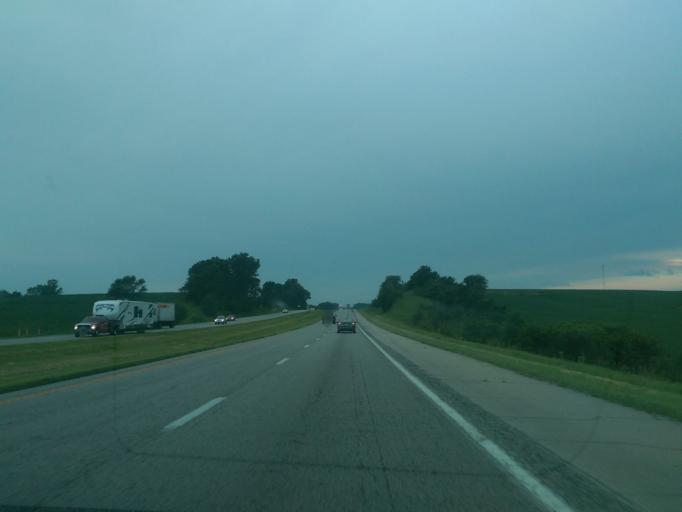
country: US
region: Missouri
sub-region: Holt County
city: Oregon
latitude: 40.0594
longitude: -95.1646
